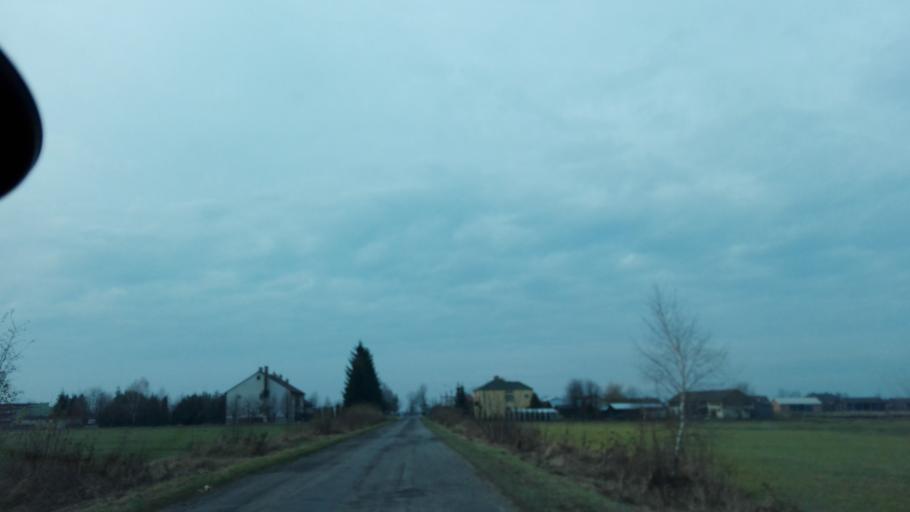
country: PL
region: Lublin Voivodeship
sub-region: Powiat bialski
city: Sosnowka
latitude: 51.7497
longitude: 23.3447
